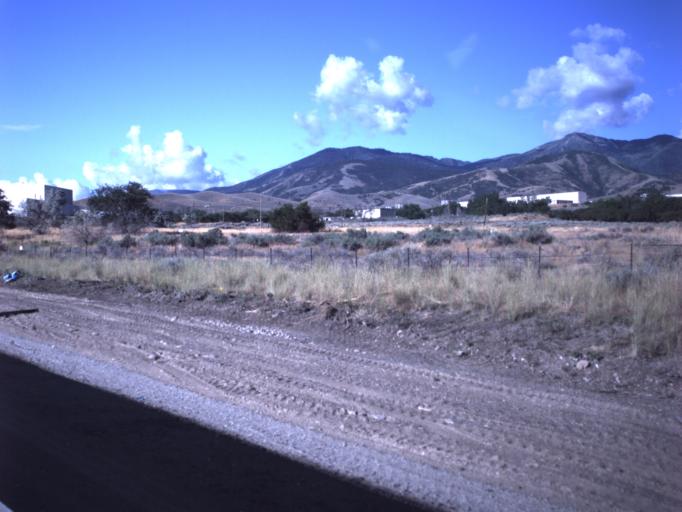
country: US
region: Utah
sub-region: Salt Lake County
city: Magna
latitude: 40.6694
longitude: -112.0920
